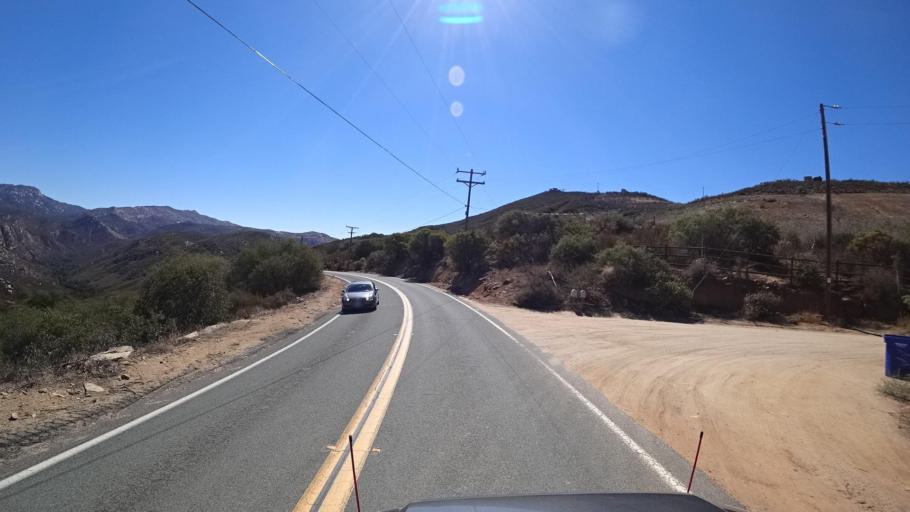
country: US
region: California
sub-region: San Diego County
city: Descanso
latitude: 32.7543
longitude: -116.6750
